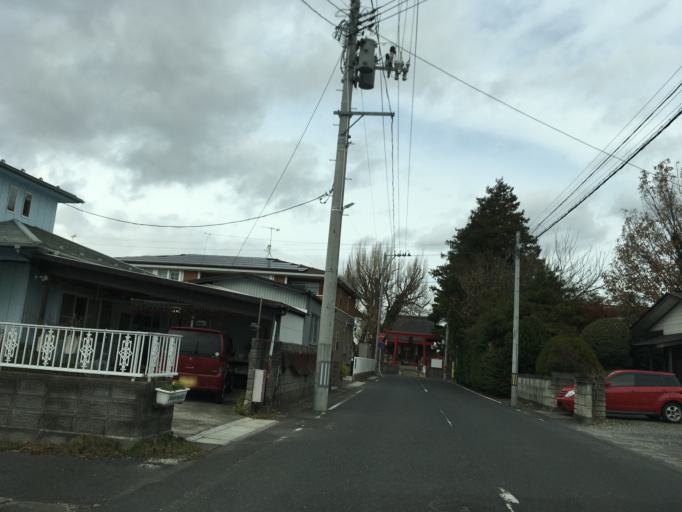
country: JP
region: Miyagi
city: Wakuya
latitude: 38.6916
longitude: 141.1986
